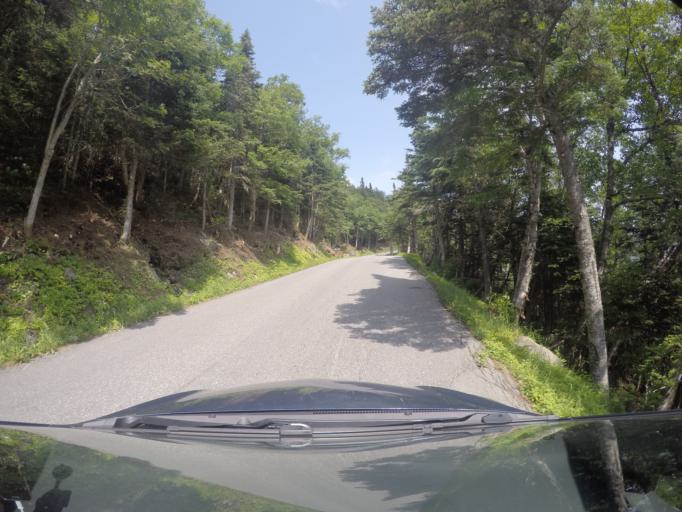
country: US
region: New Hampshire
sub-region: Coos County
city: Gorham
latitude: 44.2899
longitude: -71.2733
